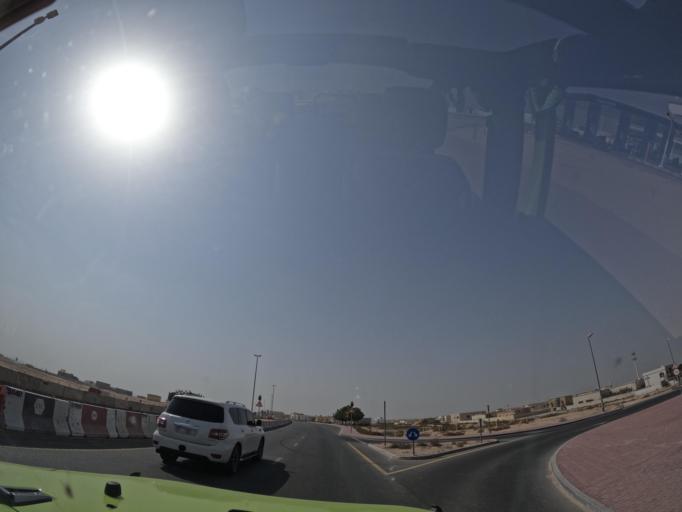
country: AE
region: Ash Shariqah
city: Sharjah
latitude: 25.1979
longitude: 55.4326
